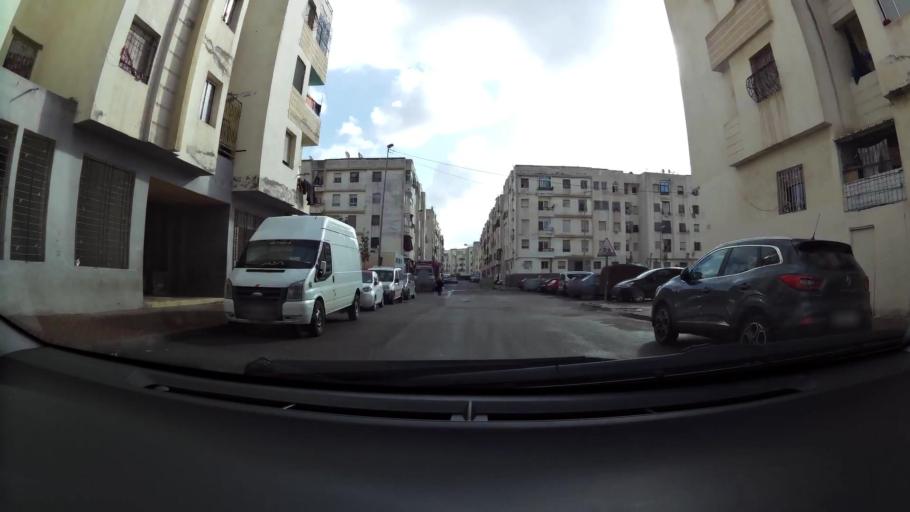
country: MA
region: Grand Casablanca
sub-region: Mediouna
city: Tit Mellil
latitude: 33.5946
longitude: -7.5386
